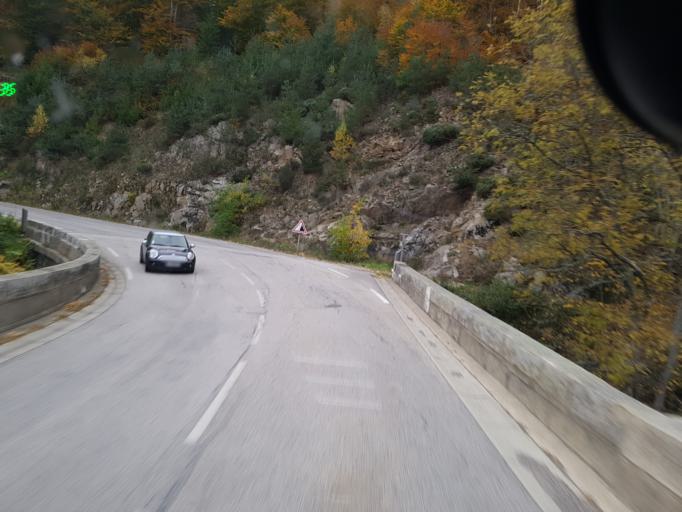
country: FR
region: Auvergne
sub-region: Departement de la Haute-Loire
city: Lapte
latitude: 45.1634
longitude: 4.1699
